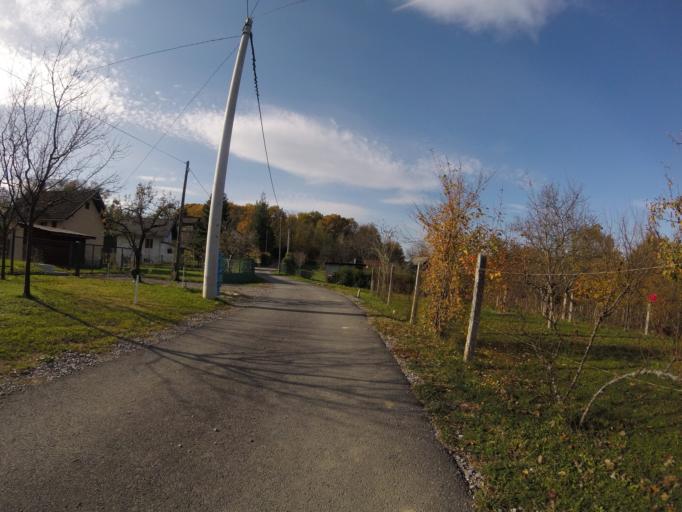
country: HR
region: Zagrebacka
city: Gradici
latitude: 45.6267
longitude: 16.0166
